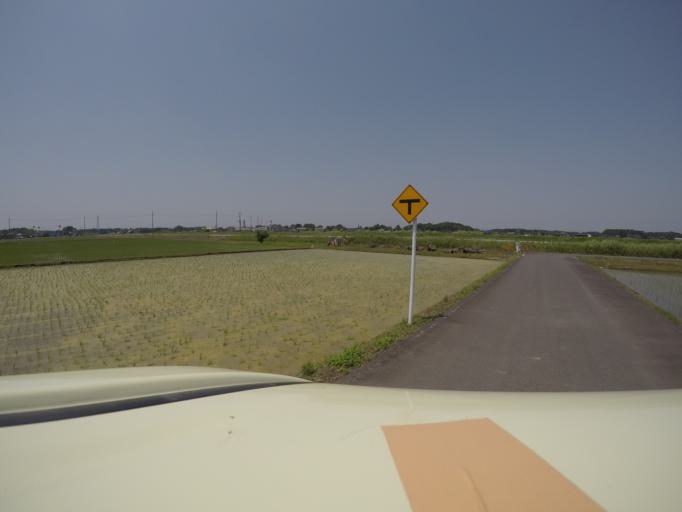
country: JP
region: Ibaraki
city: Mitsukaido
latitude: 36.0321
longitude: 139.9575
